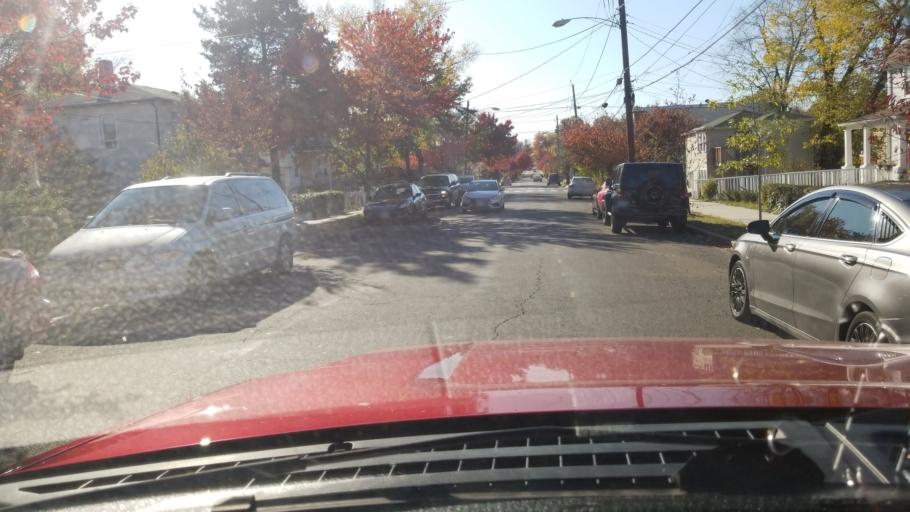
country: US
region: Maryland
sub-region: Prince George's County
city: Fairmount Heights
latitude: 38.9022
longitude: -76.9392
